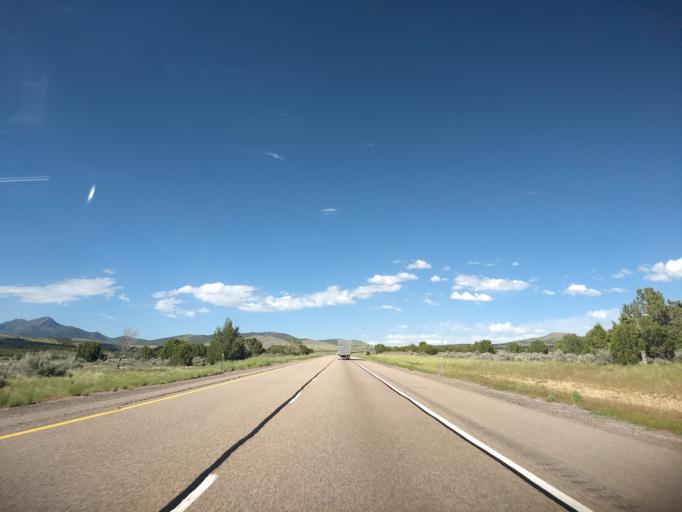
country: US
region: Utah
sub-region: Millard County
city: Fillmore
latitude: 39.1631
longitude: -112.2203
